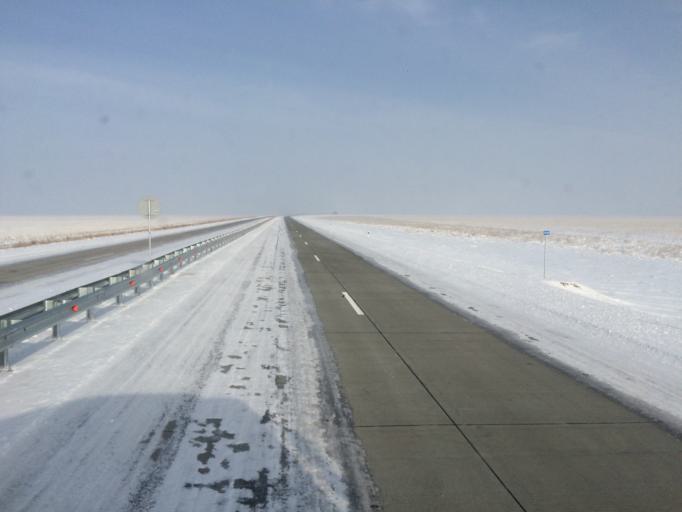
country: KG
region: Chuy
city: Sokuluk
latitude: 43.3374
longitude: 74.2831
